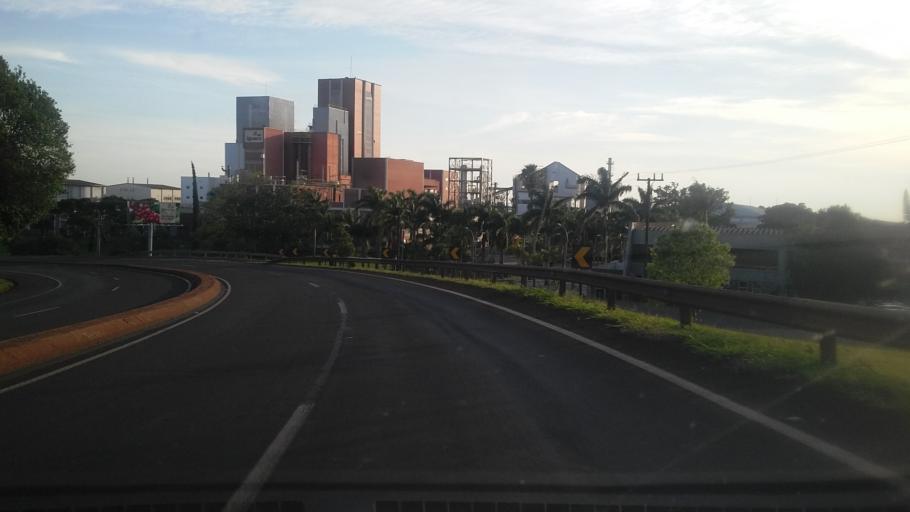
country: BR
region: Parana
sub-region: Assai
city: Assai
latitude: -23.1883
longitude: -50.6397
